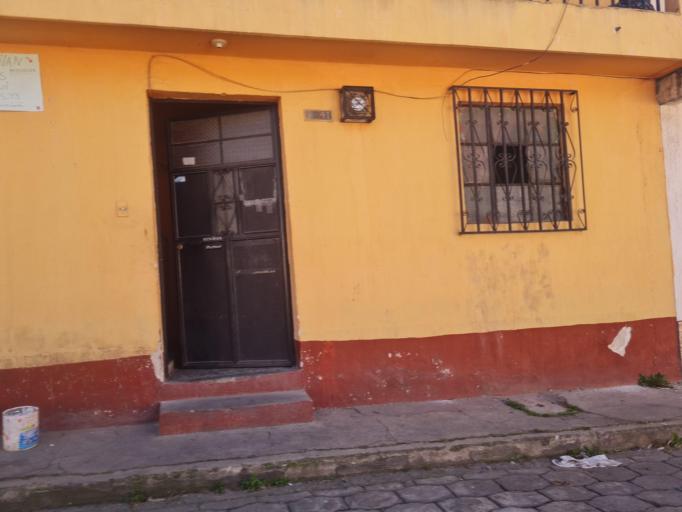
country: GT
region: Quetzaltenango
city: Quetzaltenango
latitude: 14.8418
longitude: -91.5336
